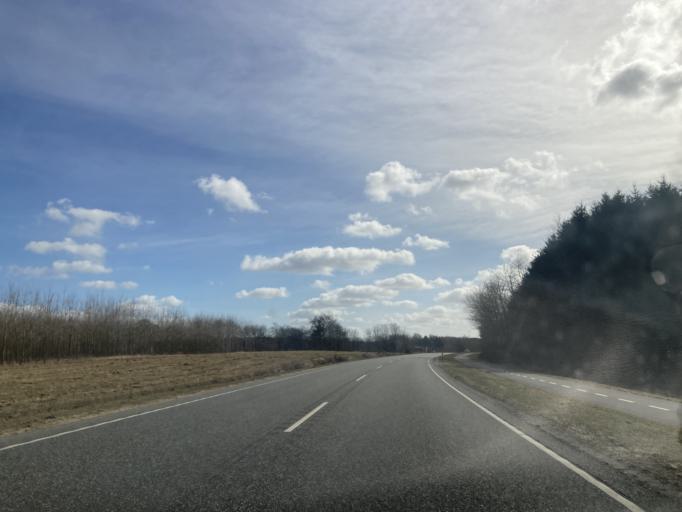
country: DK
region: Central Jutland
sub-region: Hedensted Kommune
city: Torring
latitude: 55.9851
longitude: 9.3920
